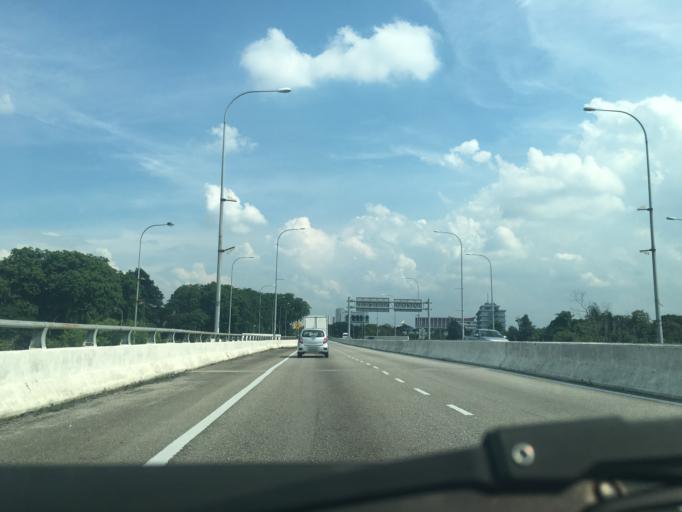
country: MY
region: Perak
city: Ipoh
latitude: 4.6106
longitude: 101.0786
